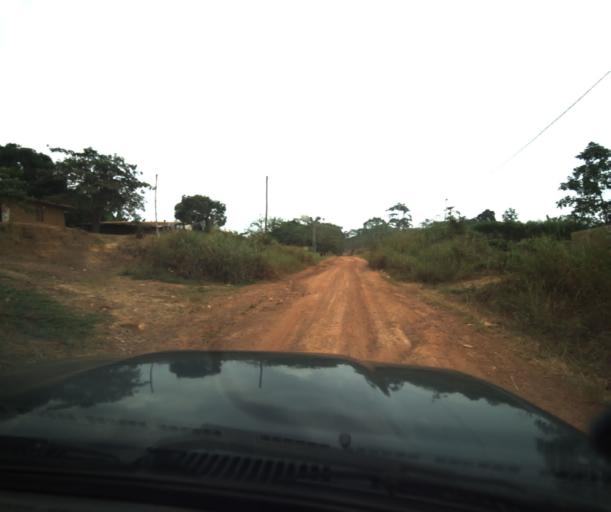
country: CM
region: Centre
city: Akono
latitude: 3.5012
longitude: 11.3345
